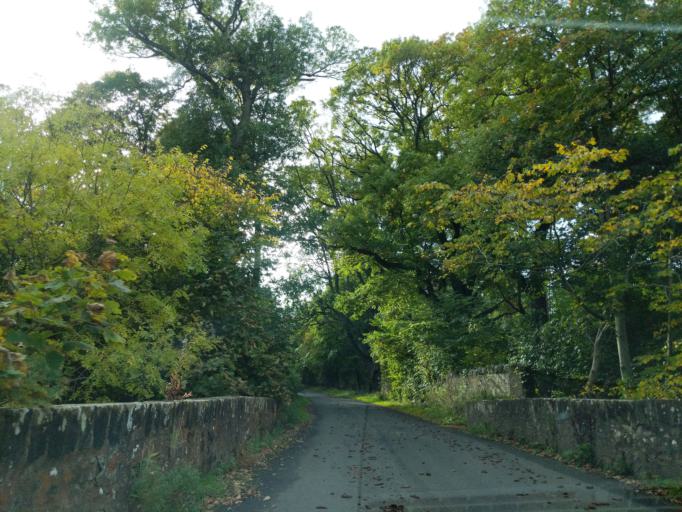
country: GB
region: Scotland
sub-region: East Lothian
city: Haddington
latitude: 55.9332
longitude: -2.7782
